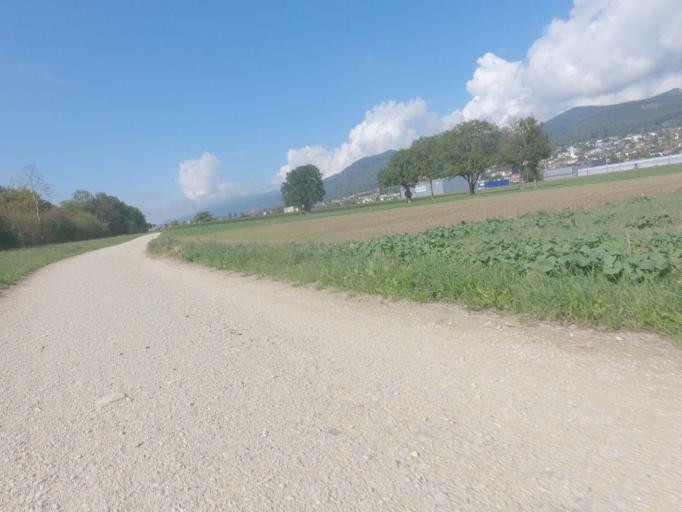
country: CH
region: Solothurn
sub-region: Bezirk Olten
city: Wangen
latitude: 47.3329
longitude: 7.8592
